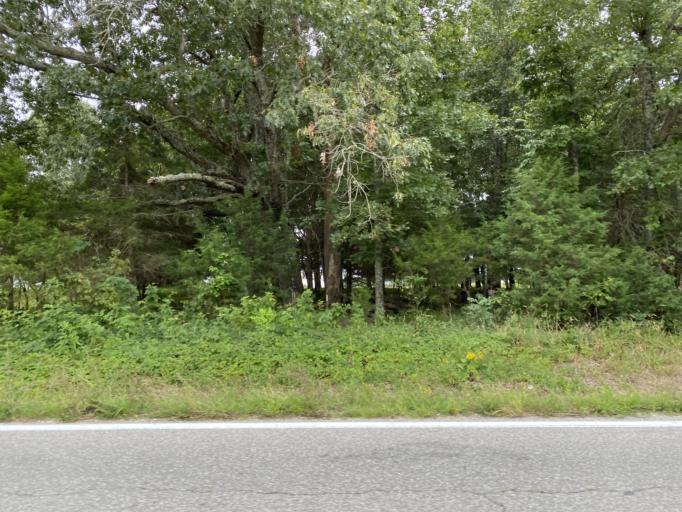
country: US
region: Arkansas
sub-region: Fulton County
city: Salem
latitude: 36.4175
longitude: -91.7206
